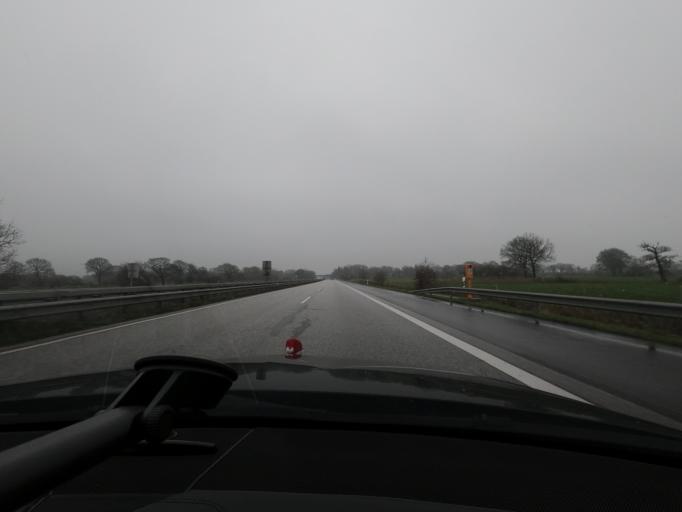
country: DE
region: Schleswig-Holstein
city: Schulldorf
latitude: 54.2906
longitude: 9.7646
